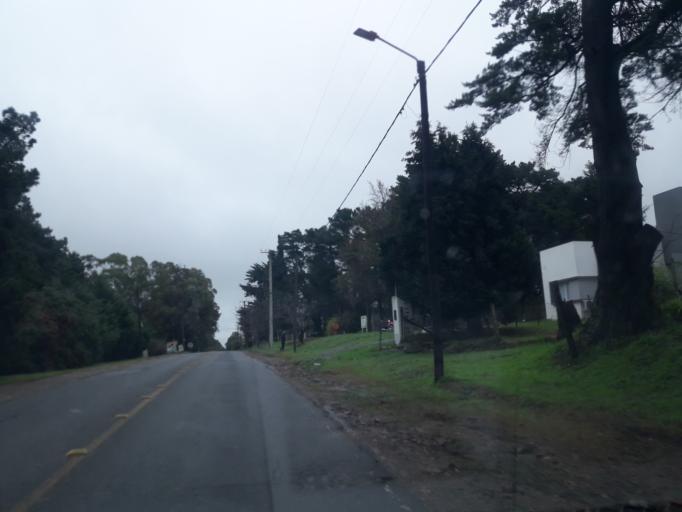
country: AR
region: Buenos Aires
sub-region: Partido de Tandil
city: Tandil
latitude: -37.3297
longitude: -59.1770
